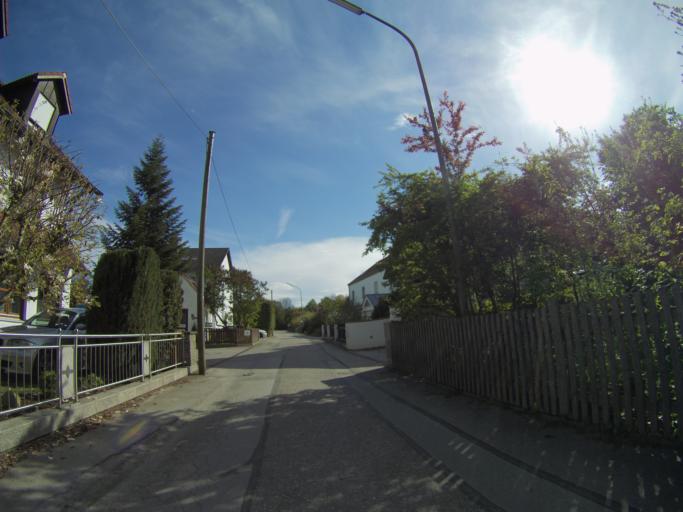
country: DE
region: Bavaria
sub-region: Upper Bavaria
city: Freising
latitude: 48.4261
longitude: 11.7334
